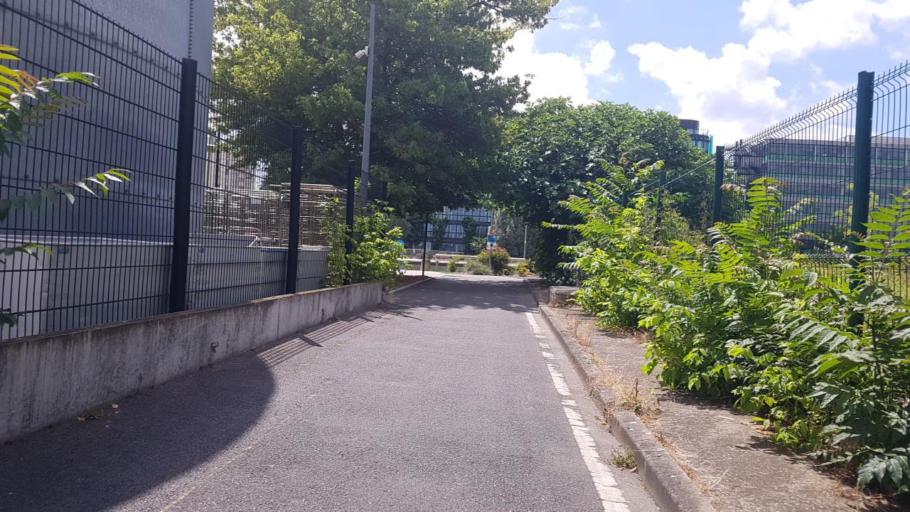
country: FR
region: Ile-de-France
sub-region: Departement de Seine-Saint-Denis
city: Pantin
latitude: 48.8956
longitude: 2.4150
